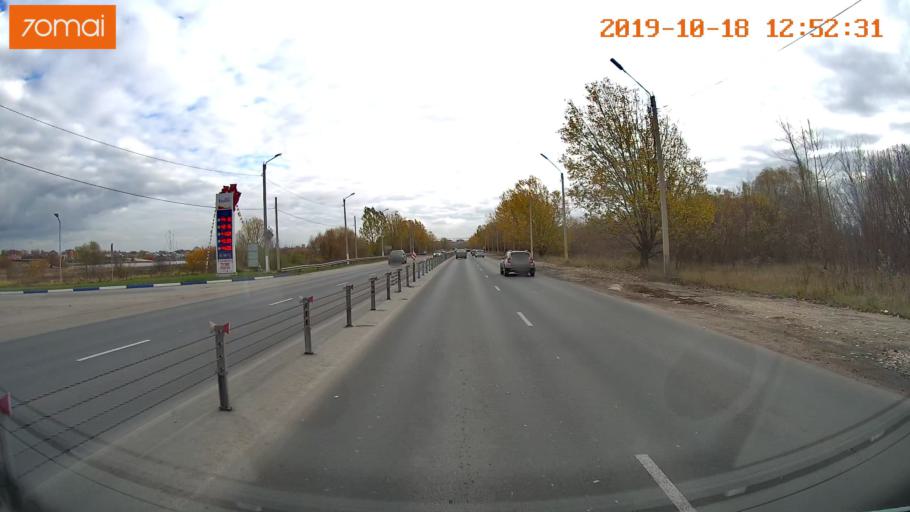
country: RU
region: Rjazan
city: Ryazan'
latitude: 54.6517
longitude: 39.6948
